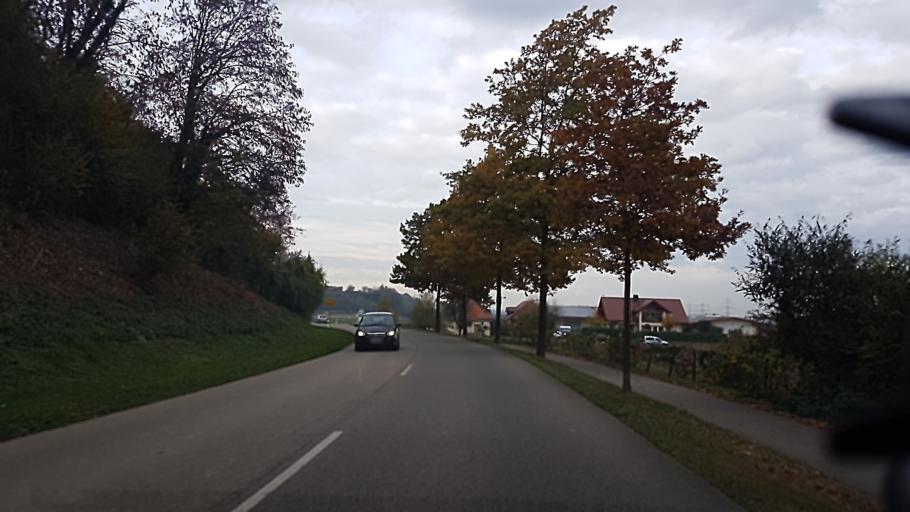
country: DE
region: Baden-Wuerttemberg
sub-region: Freiburg Region
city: Eichstetten
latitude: 48.0971
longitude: 7.7454
